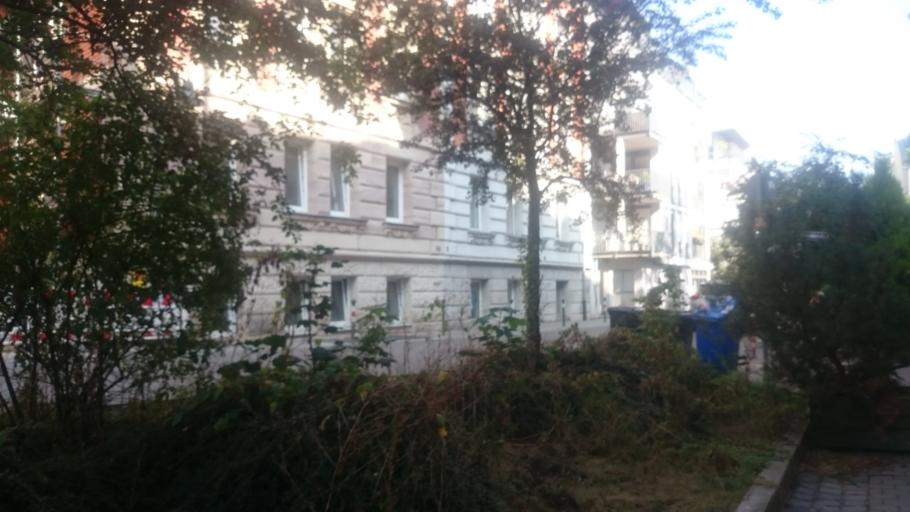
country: DE
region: Bavaria
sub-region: Regierungsbezirk Mittelfranken
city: Nuernberg
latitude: 49.4571
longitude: 11.0635
